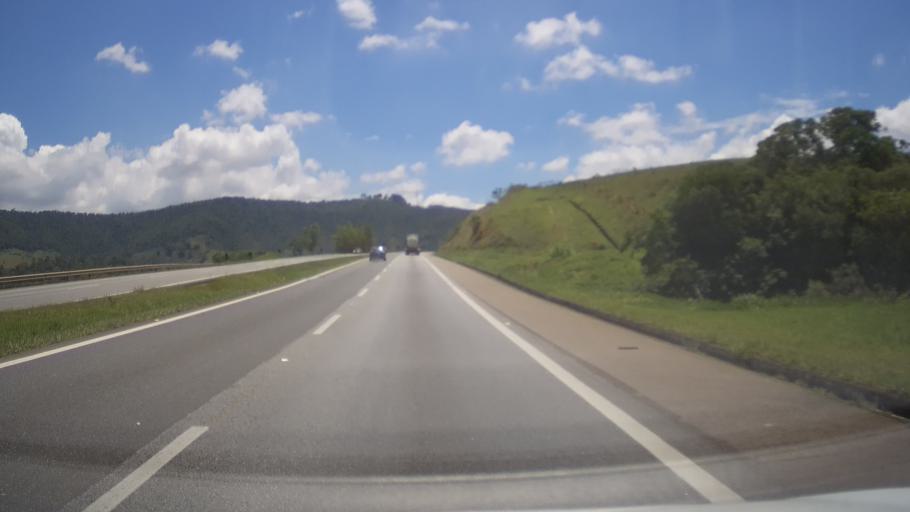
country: BR
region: Minas Gerais
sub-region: Campanha
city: Campanha
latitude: -21.8186
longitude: -45.4930
